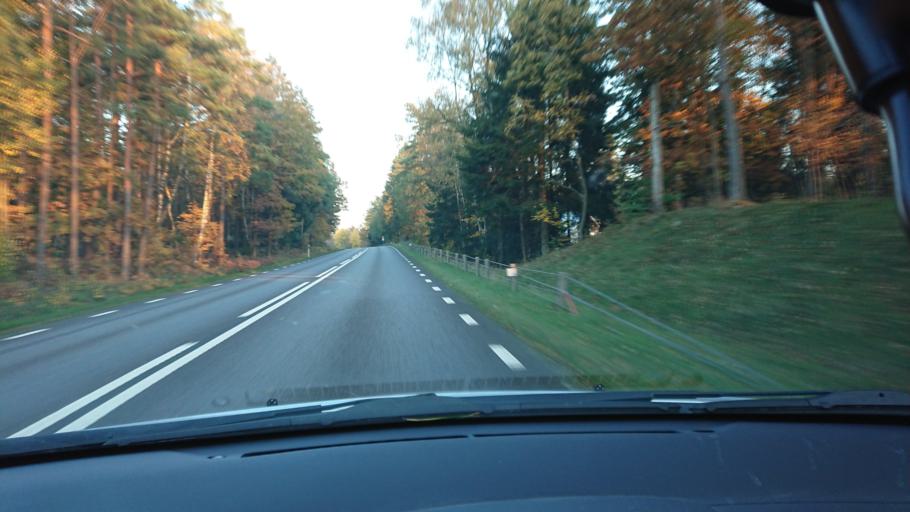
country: SE
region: Halland
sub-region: Halmstads Kommun
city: Oskarstrom
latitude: 56.7079
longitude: 13.0573
